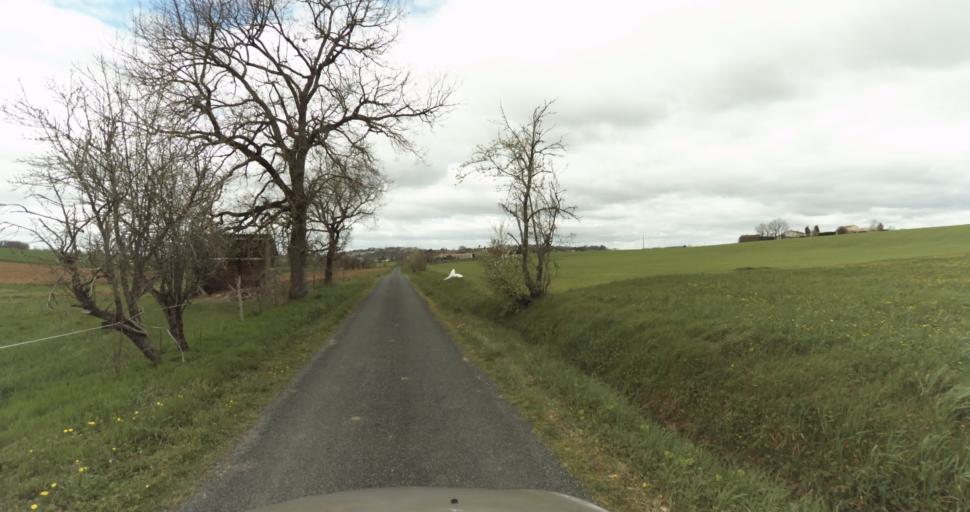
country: FR
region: Midi-Pyrenees
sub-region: Departement du Tarn
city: Puygouzon
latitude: 43.8748
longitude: 2.1730
